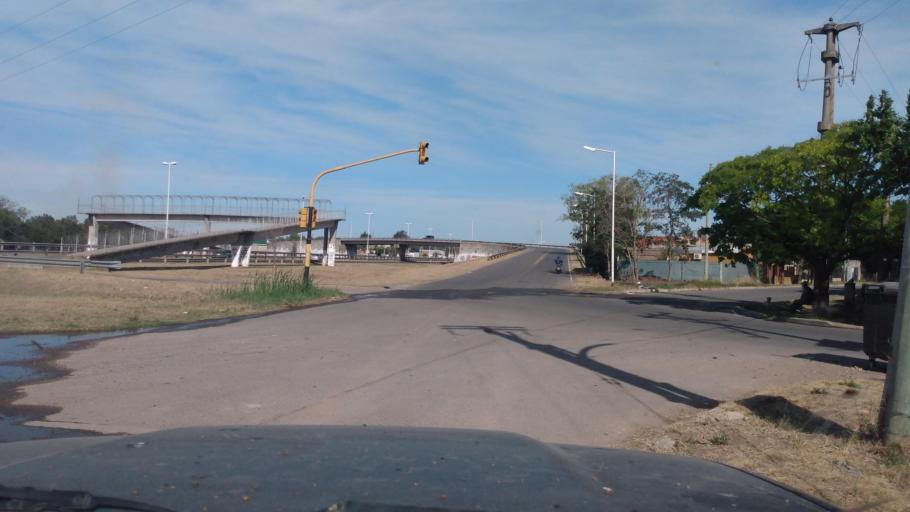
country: AR
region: Buenos Aires
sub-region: Partido de Lujan
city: Lujan
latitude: -34.5517
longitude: -59.1103
